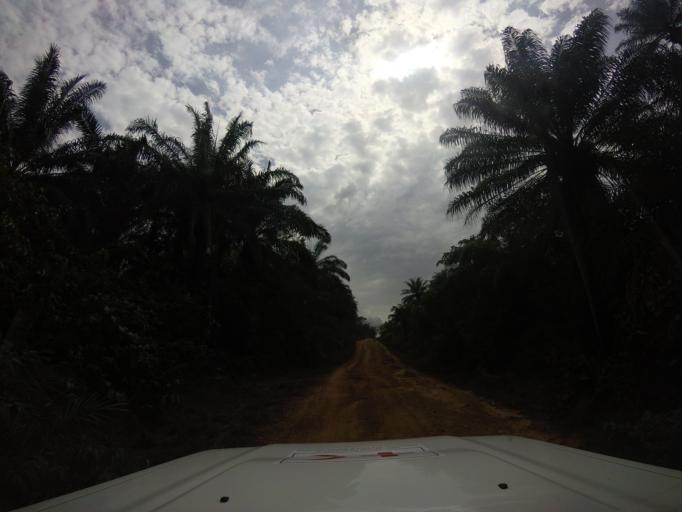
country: SL
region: Southern Province
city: Zimmi
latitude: 7.2107
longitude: -11.2014
